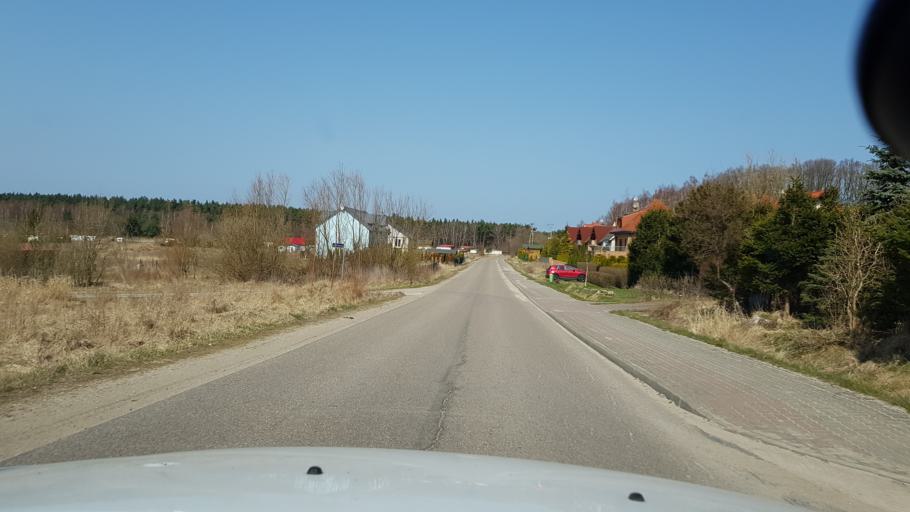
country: PL
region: West Pomeranian Voivodeship
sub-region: Powiat slawienski
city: Darlowo
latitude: 54.5154
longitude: 16.5157
